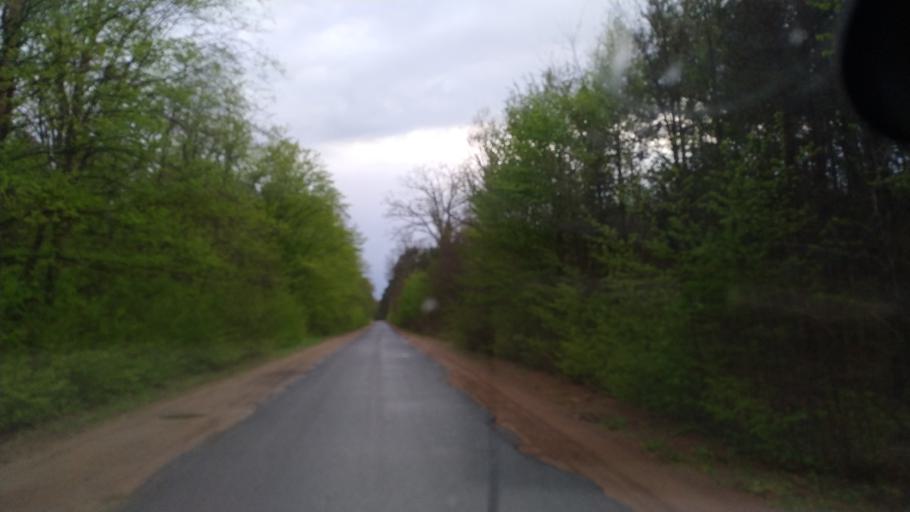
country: PL
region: Pomeranian Voivodeship
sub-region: Powiat starogardzki
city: Osiek
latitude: 53.7061
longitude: 18.5760
